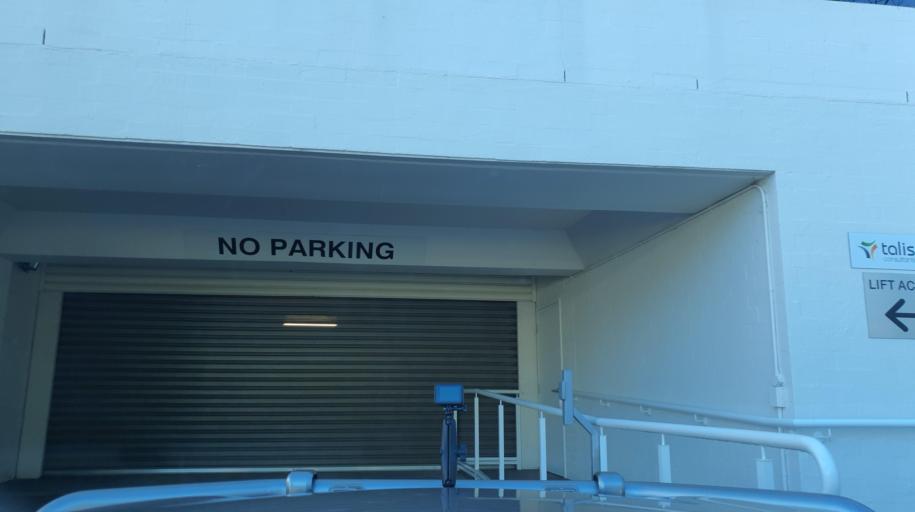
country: AU
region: Western Australia
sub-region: Vincent
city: Leederville
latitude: -31.9388
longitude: 115.8453
